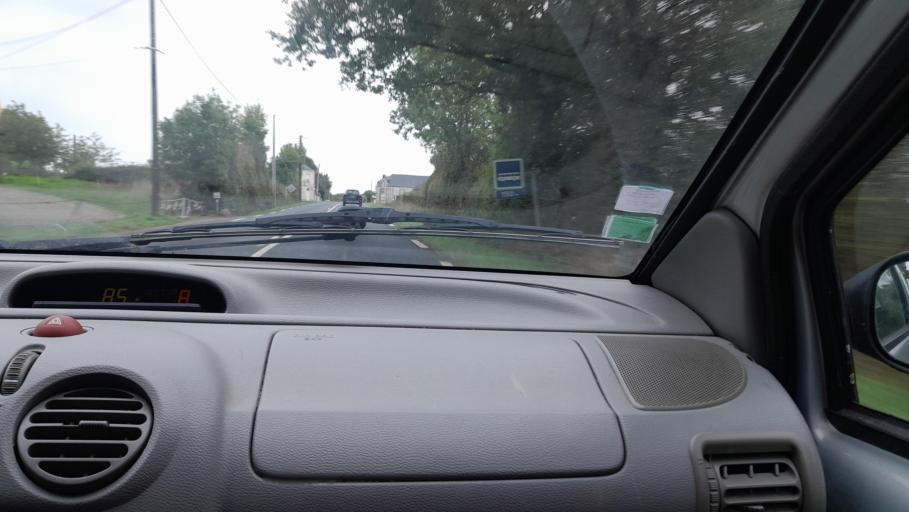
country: FR
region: Pays de la Loire
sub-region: Departement de la Loire-Atlantique
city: Saint-Mars-la-Jaille
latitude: 47.4866
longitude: -1.1737
